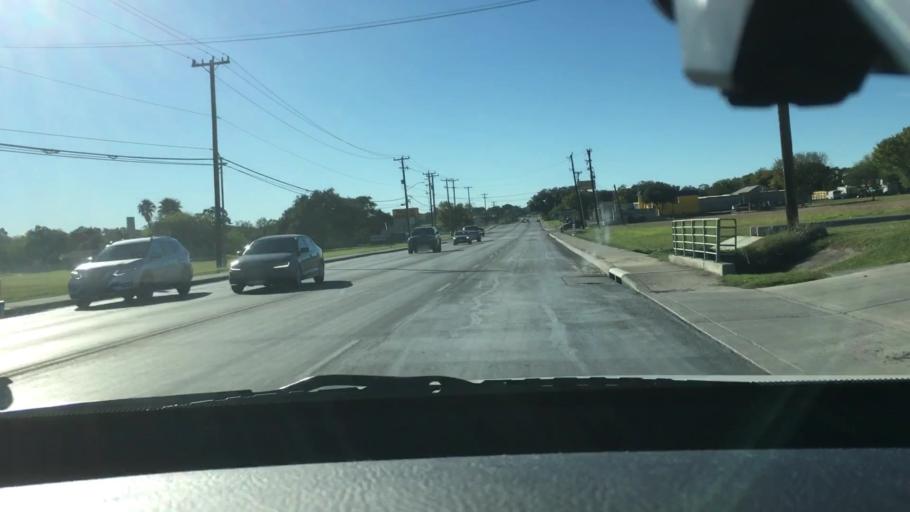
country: US
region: Texas
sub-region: Bexar County
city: Converse
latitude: 29.5217
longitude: -98.3476
